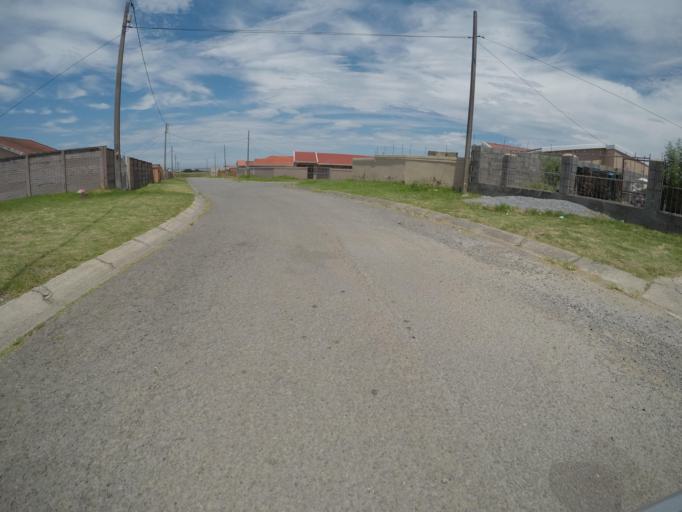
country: ZA
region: Eastern Cape
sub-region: Buffalo City Metropolitan Municipality
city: East London
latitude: -33.0482
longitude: 27.8507
